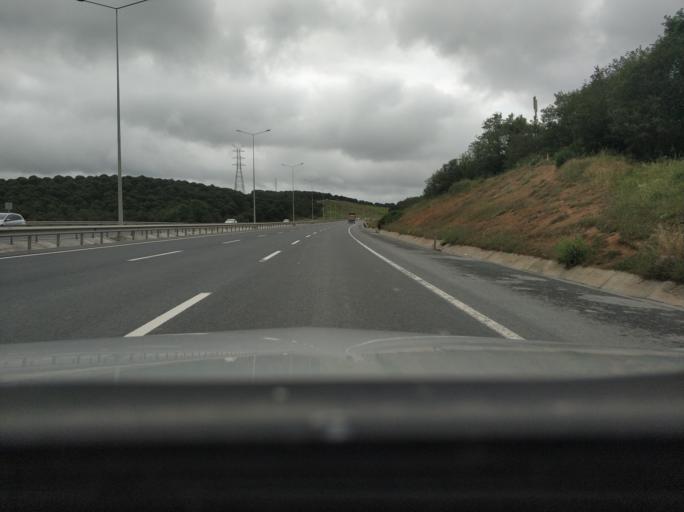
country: TR
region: Istanbul
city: Kemerburgaz
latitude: 41.1433
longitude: 28.9060
